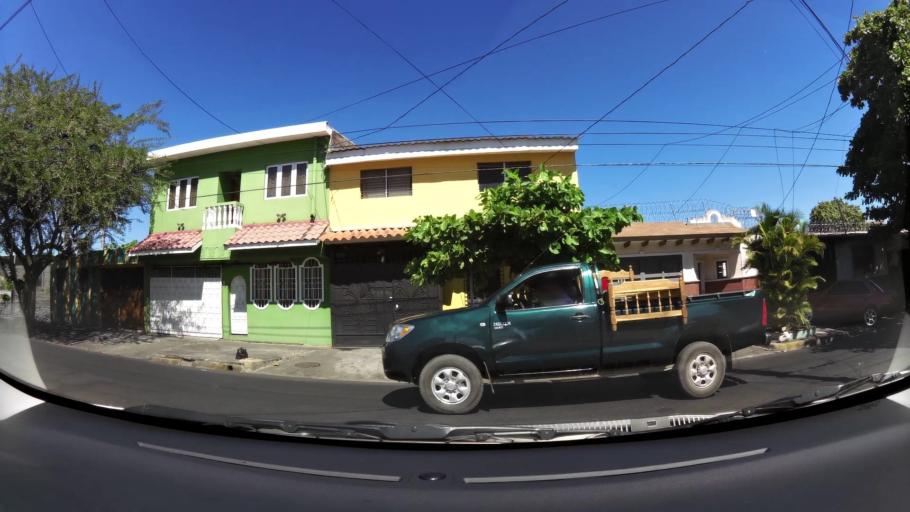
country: SV
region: San Miguel
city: San Miguel
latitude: 13.4788
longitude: -88.1670
